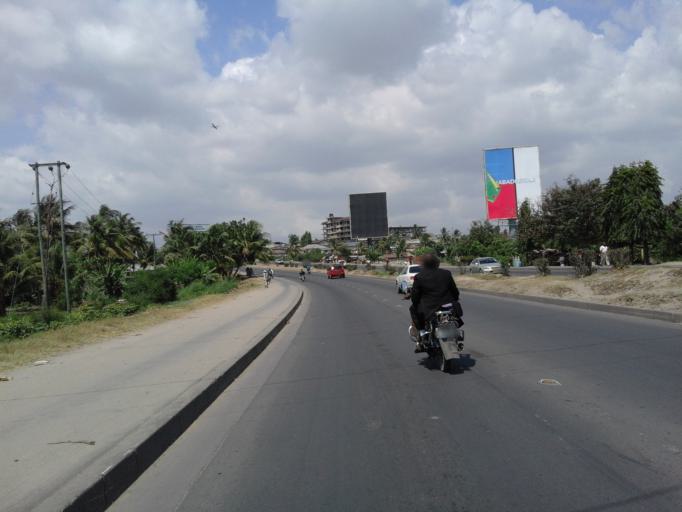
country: TZ
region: Dar es Salaam
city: Magomeni
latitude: -6.8132
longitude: 39.2547
